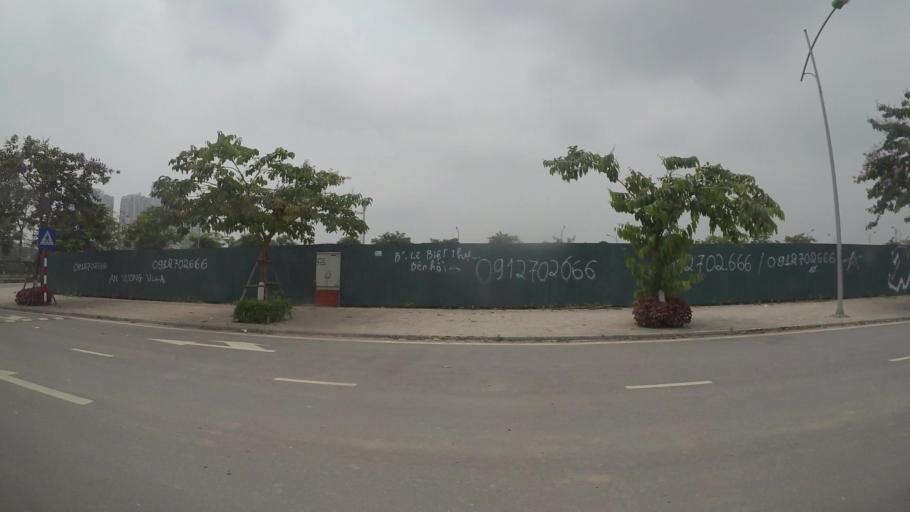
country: VN
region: Ha Noi
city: Ha Dong
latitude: 20.9800
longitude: 105.7563
